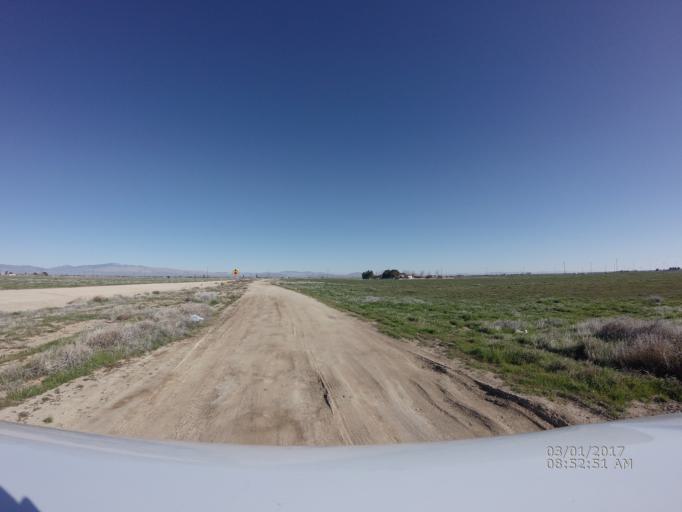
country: US
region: California
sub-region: Los Angeles County
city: Quartz Hill
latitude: 34.7304
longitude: -118.2723
